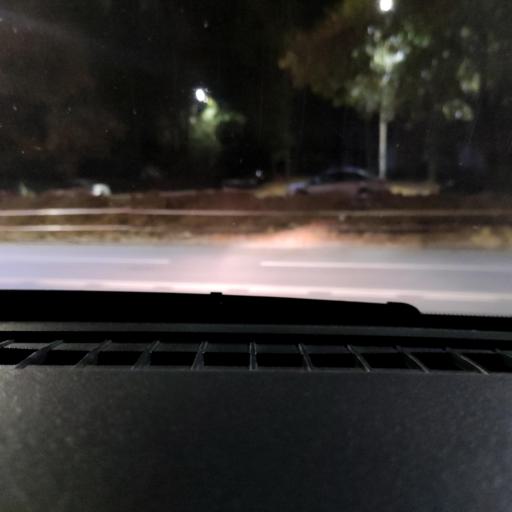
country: RU
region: Voronezj
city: Podgornoye
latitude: 51.7133
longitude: 39.1619
